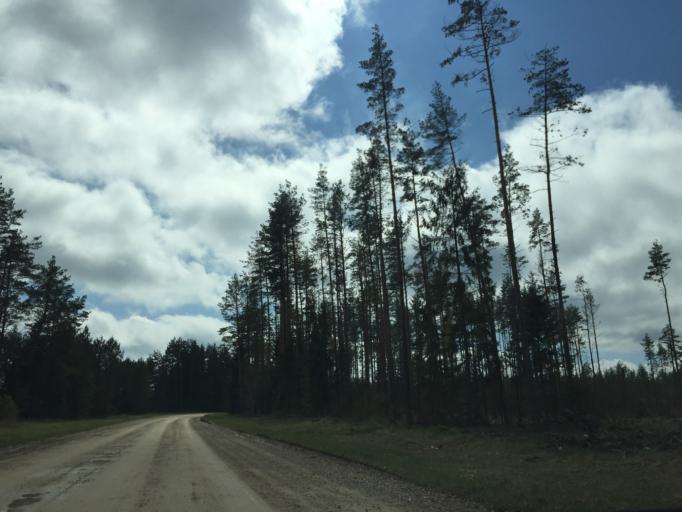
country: EE
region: Valgamaa
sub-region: Valga linn
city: Valga
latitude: 57.6338
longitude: 26.2351
